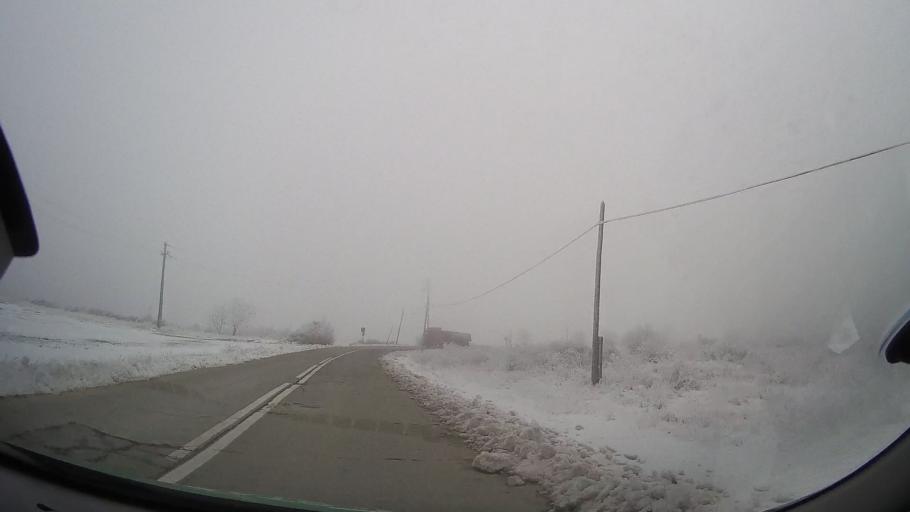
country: RO
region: Bacau
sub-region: Comuna Podu Turcului
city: Podu Turcului
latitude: 46.2102
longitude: 27.4243
